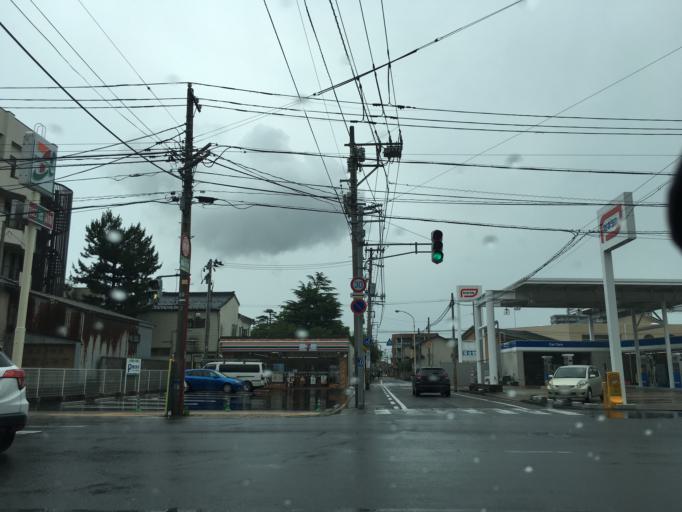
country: JP
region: Niigata
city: Niigata-shi
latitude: 37.9150
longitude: 139.0658
